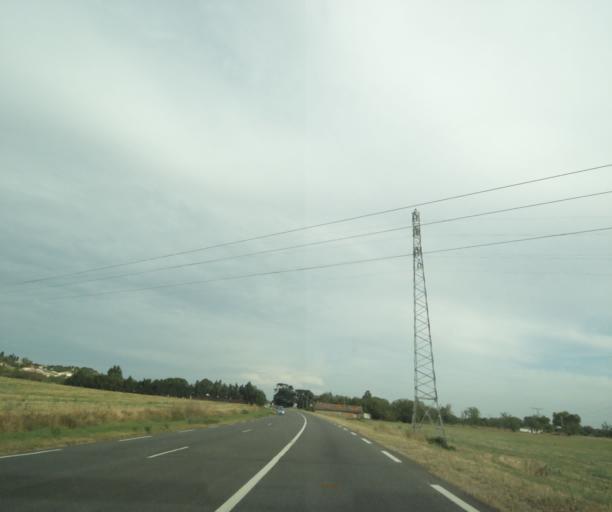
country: FR
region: Midi-Pyrenees
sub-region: Departement de la Haute-Garonne
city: Castelnau-d'Estretefonds
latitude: 43.7922
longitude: 1.3385
